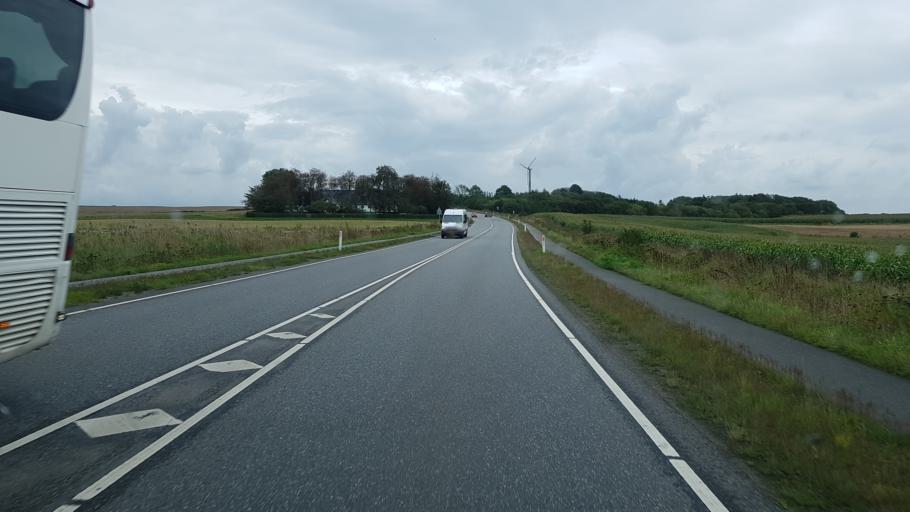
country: DK
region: Central Jutland
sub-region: Horsens Kommune
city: Braedstrup
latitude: 55.9179
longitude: 9.6974
